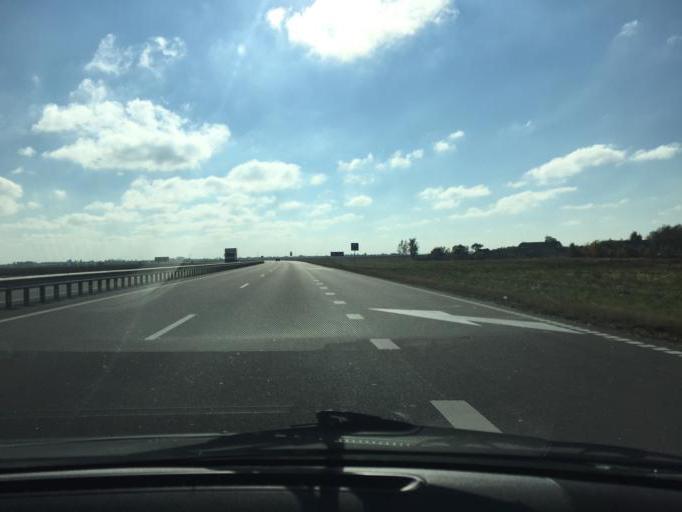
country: BY
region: Minsk
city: Slutsk
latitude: 53.1424
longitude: 27.5520
